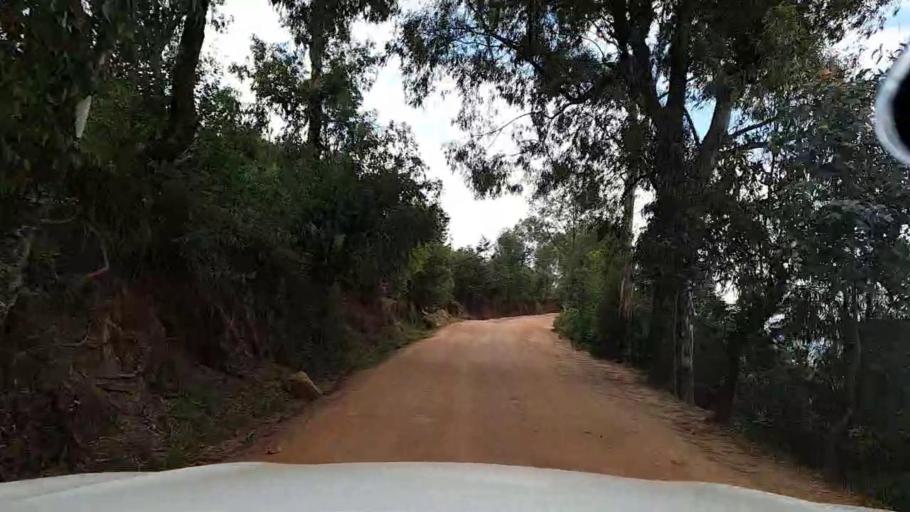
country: RW
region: Southern Province
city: Nzega
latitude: -2.7100
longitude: 29.5237
